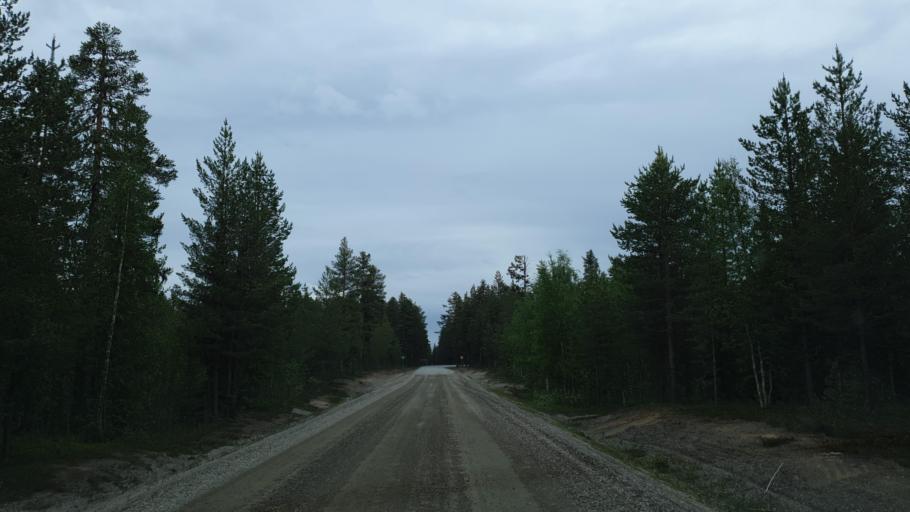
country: SE
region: Vaesterbotten
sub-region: Sorsele Kommun
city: Sorsele
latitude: 65.5529
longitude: 17.5072
